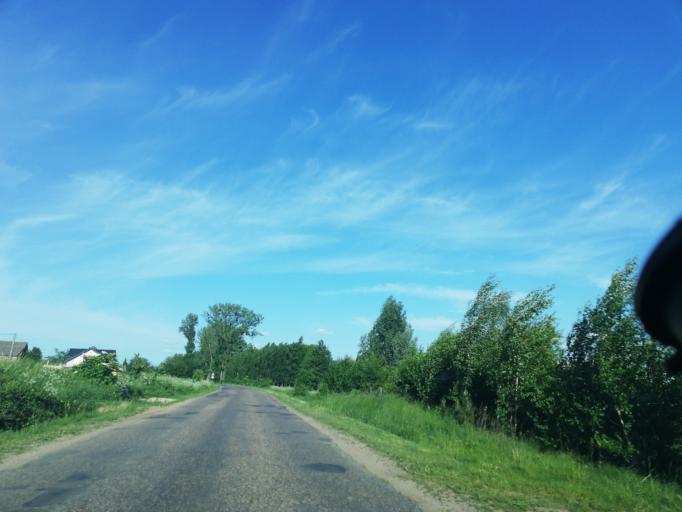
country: PL
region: Kujawsko-Pomorskie
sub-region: Powiat golubsko-dobrzynski
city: Zbojno
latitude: 53.0389
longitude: 19.0867
